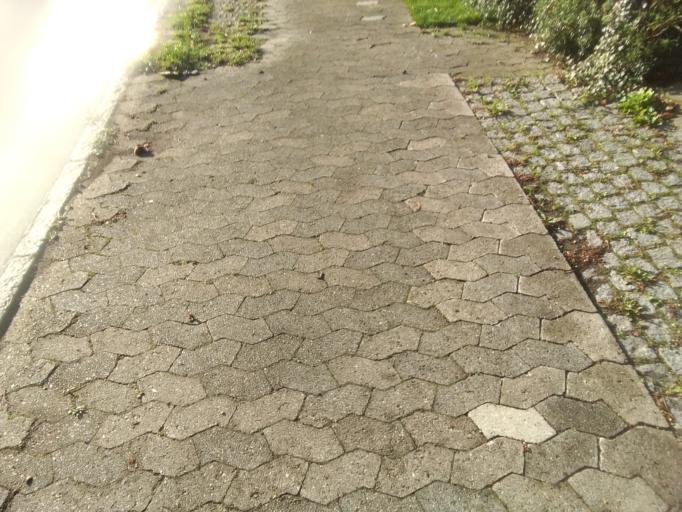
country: DK
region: Capital Region
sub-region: Gladsaxe Municipality
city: Buddinge
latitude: 55.7213
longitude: 12.5037
